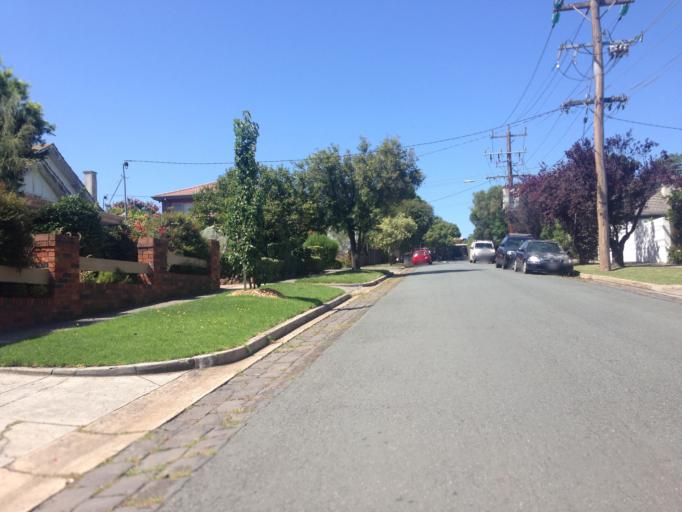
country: AU
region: Victoria
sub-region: Boroondara
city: Kew East
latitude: -37.7913
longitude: 145.0532
